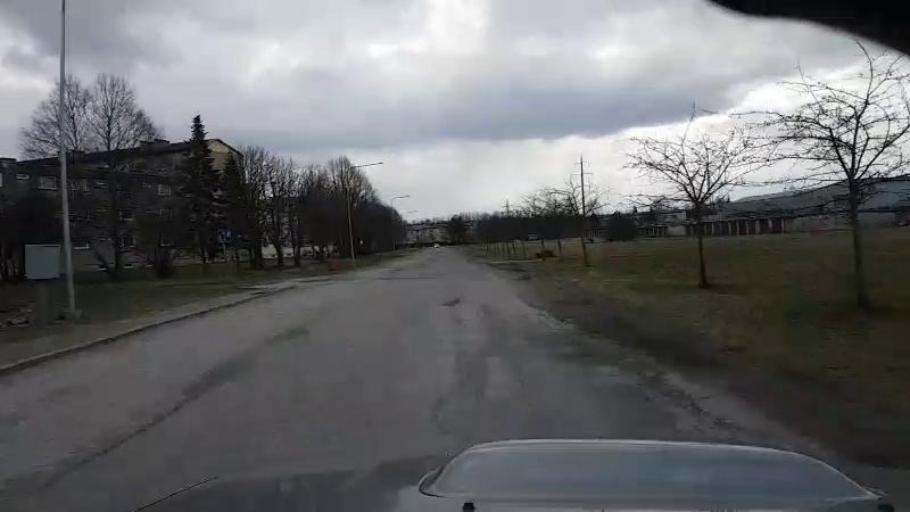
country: EE
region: Jaervamaa
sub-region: Paide linn
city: Paide
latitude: 58.8817
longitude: 25.5643
